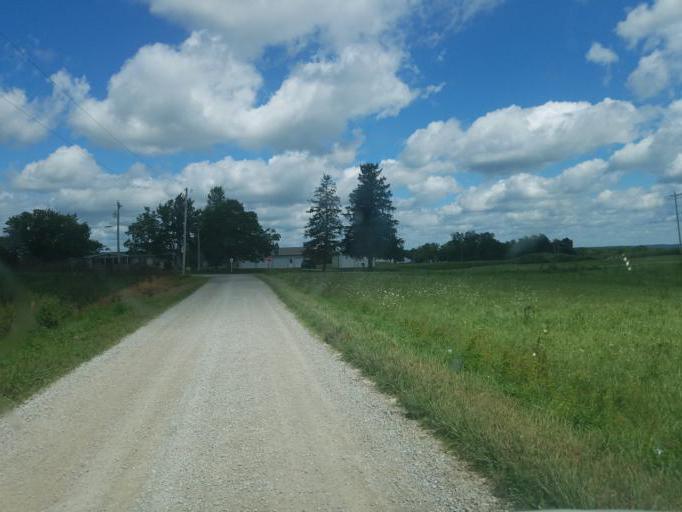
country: US
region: Ohio
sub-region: Knox County
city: Fredericktown
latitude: 40.4970
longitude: -82.6593
